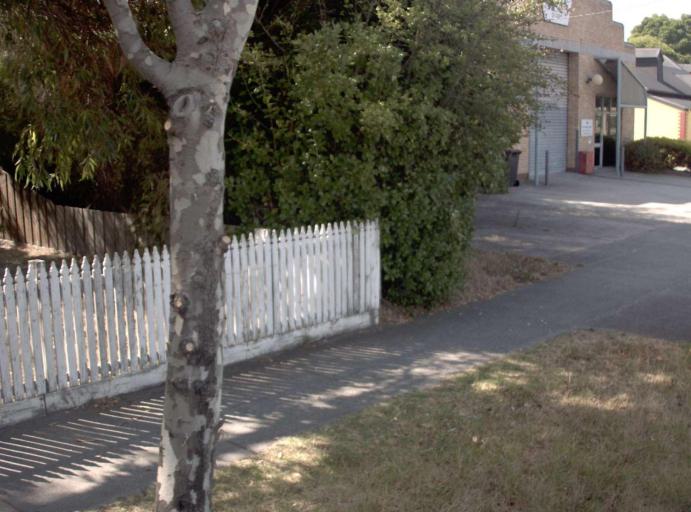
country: AU
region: Victoria
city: Hughesdale
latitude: -37.9028
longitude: 145.0864
